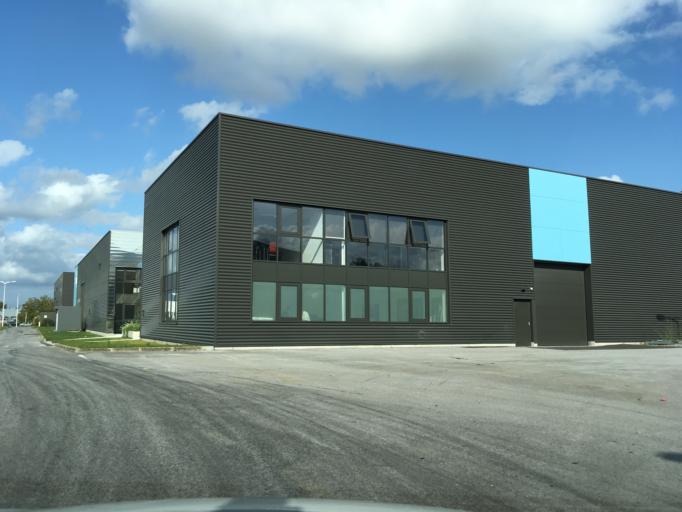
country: FR
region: Aquitaine
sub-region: Departement des Pyrenees-Atlantiques
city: Bayonne
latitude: 43.4653
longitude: -1.4926
